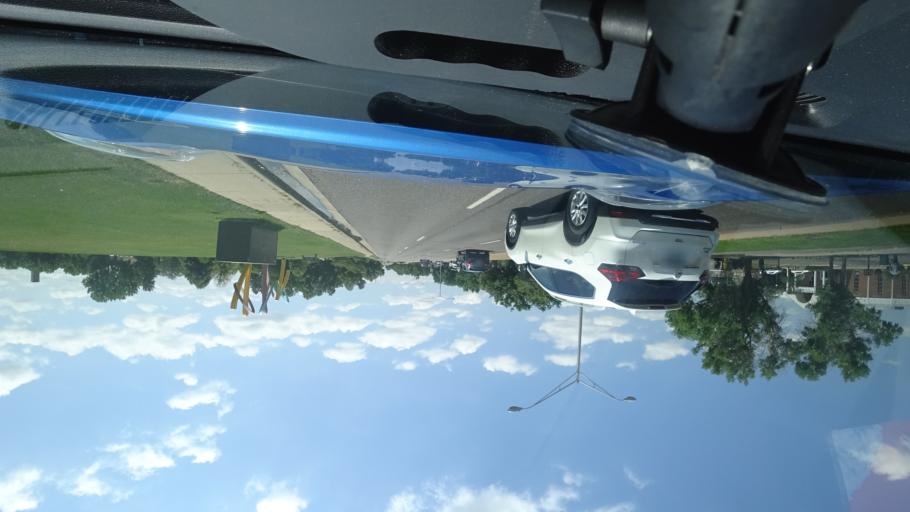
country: US
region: Colorado
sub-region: Adams County
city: Aurora
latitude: 39.7110
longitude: -104.8608
